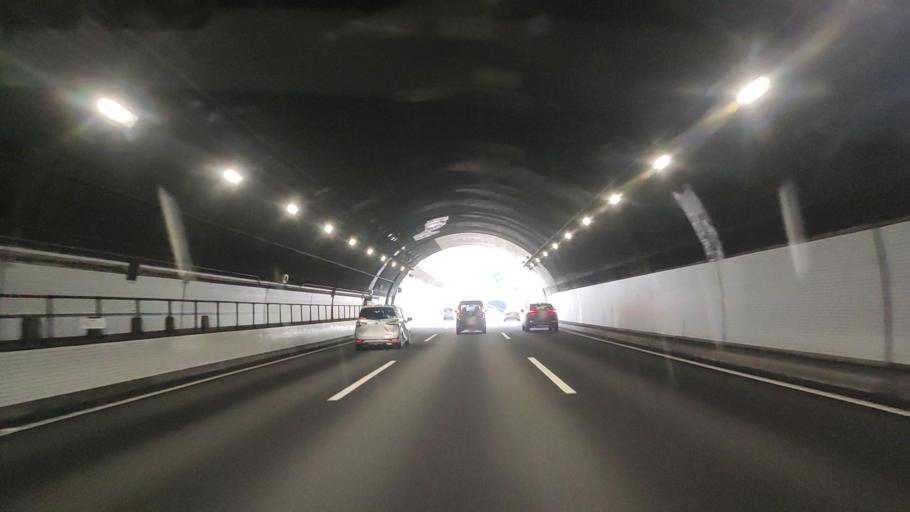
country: JP
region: Shizuoka
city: Gotemba
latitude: 35.3662
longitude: 139.0613
